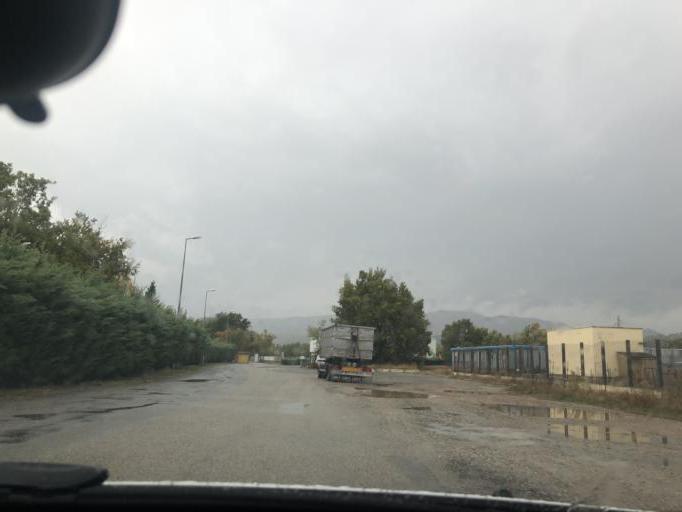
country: FR
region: Provence-Alpes-Cote d'Azur
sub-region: Departement des Alpes-de-Haute-Provence
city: Sisteron
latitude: 44.2314
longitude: 5.9163
